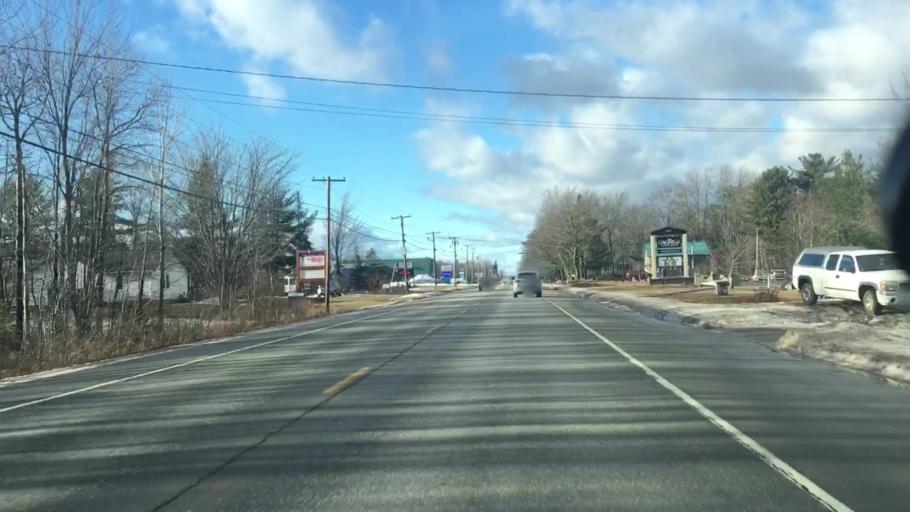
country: US
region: Maine
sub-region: Penobscot County
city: Holden
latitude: 44.7585
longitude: -68.6913
